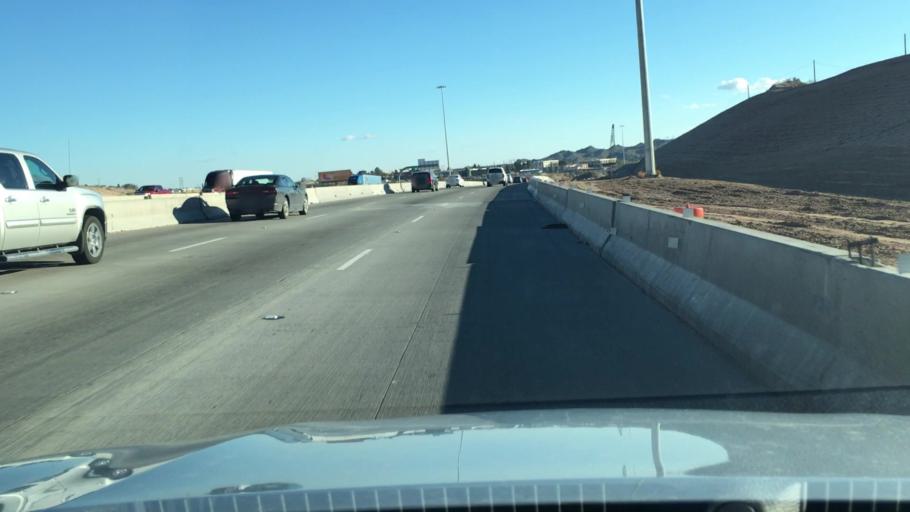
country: US
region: New Mexico
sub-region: Dona Ana County
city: Sunland Park
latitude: 31.8058
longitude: -106.5226
